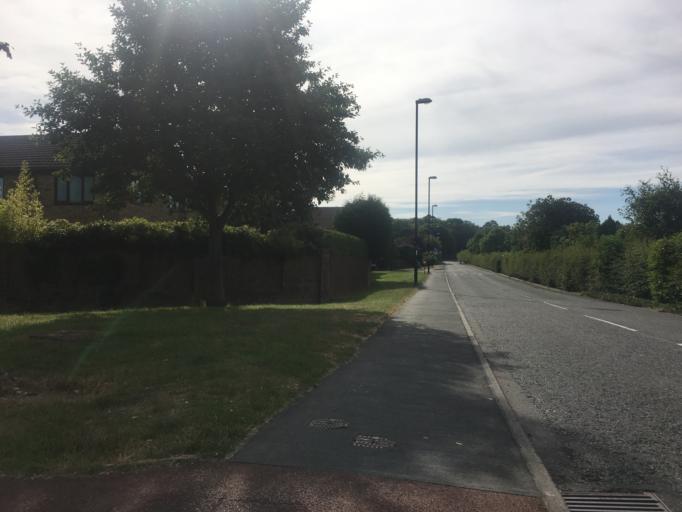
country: GB
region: England
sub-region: County Durham
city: Chester-le-Street
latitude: 54.8786
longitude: -1.5523
